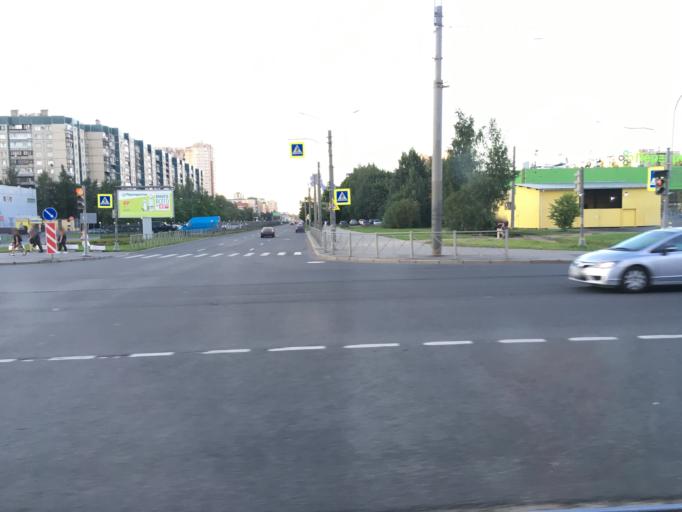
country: RU
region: St.-Petersburg
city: Komendantsky aerodrom
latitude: 60.0064
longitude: 30.2728
